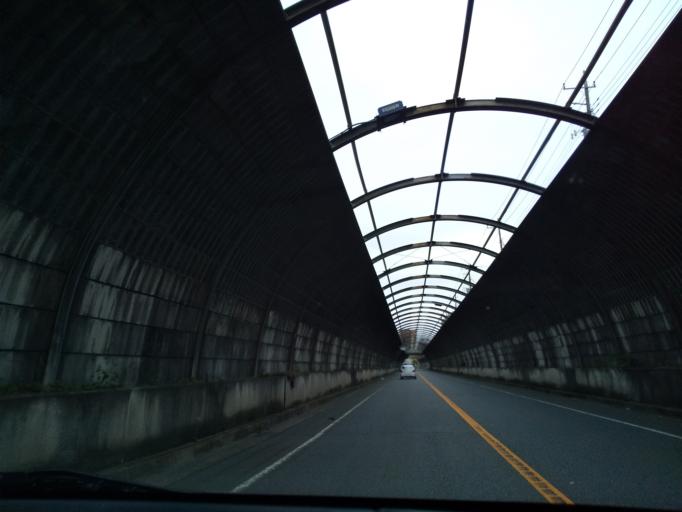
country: JP
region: Kanagawa
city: Zama
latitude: 35.5115
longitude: 139.4101
